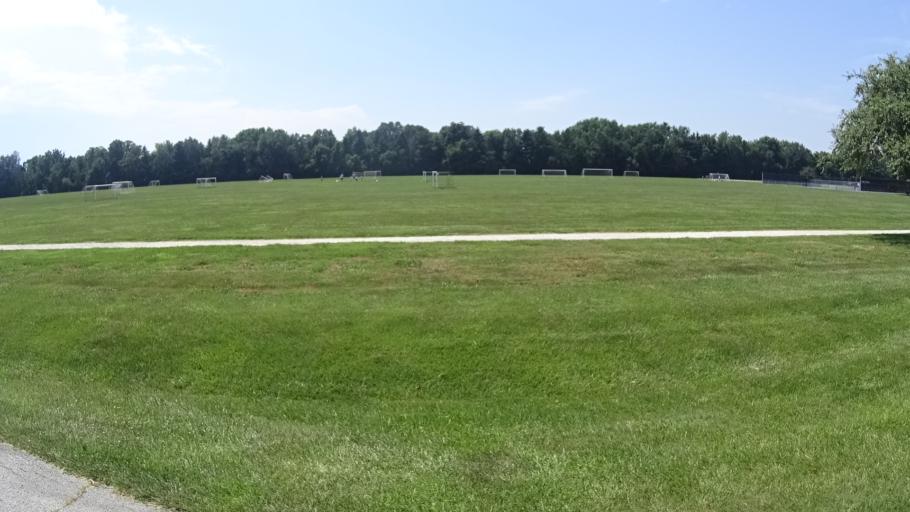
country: US
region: Ohio
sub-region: Erie County
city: Sandusky
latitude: 41.4175
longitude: -82.6359
